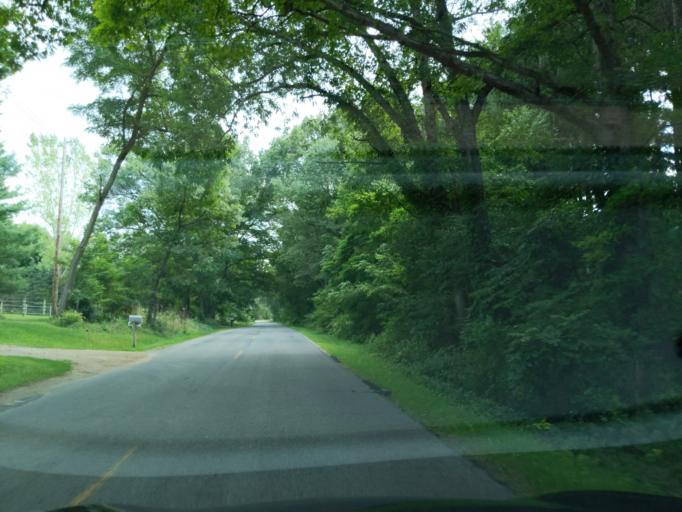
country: US
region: Michigan
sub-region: Ingham County
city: Leslie
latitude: 42.3581
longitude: -84.5464
